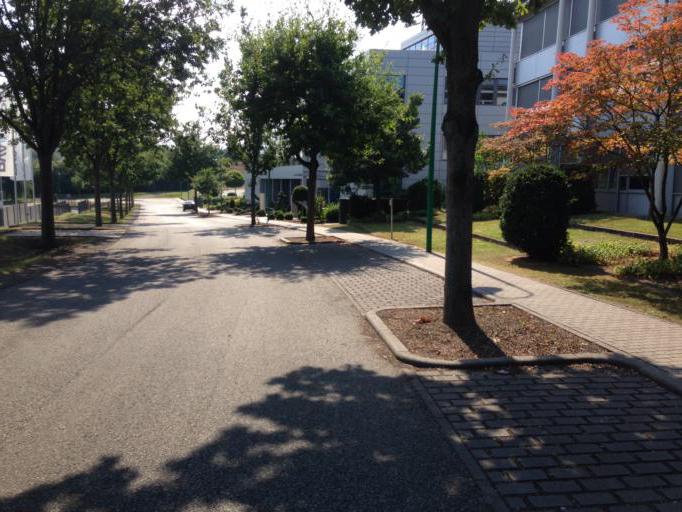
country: DE
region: Hesse
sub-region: Regierungsbezirk Giessen
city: Heuchelheim
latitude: 50.6087
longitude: 8.6485
